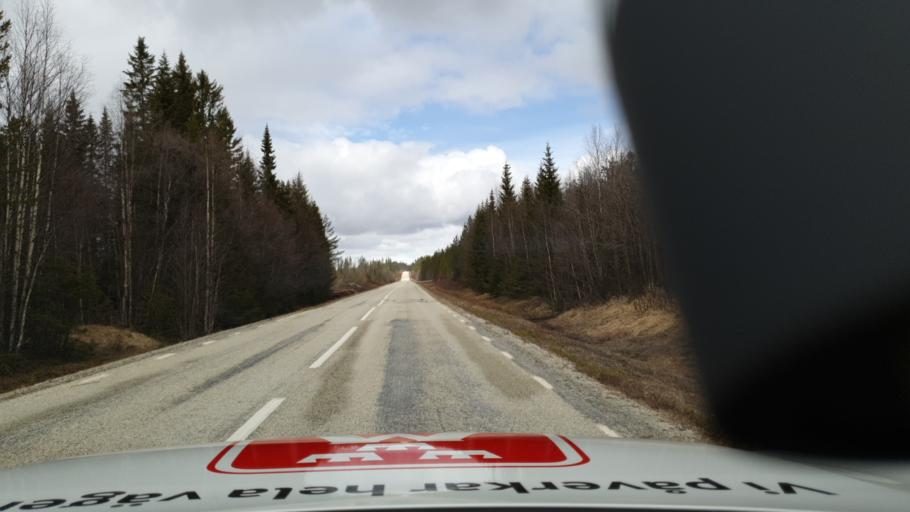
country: SE
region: Jaemtland
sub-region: Are Kommun
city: Jarpen
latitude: 62.7563
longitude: 13.7378
